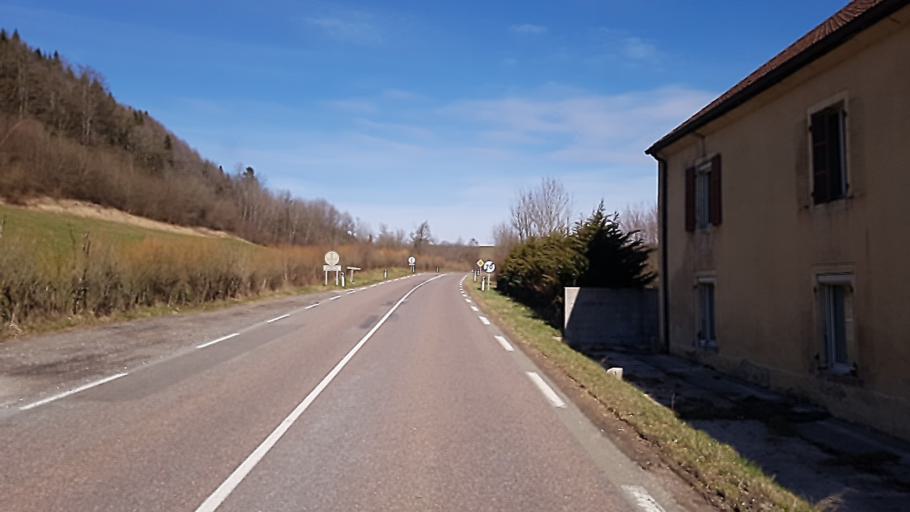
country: FR
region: Franche-Comte
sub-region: Departement du Jura
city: Champagnole
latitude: 46.6775
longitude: 5.9335
